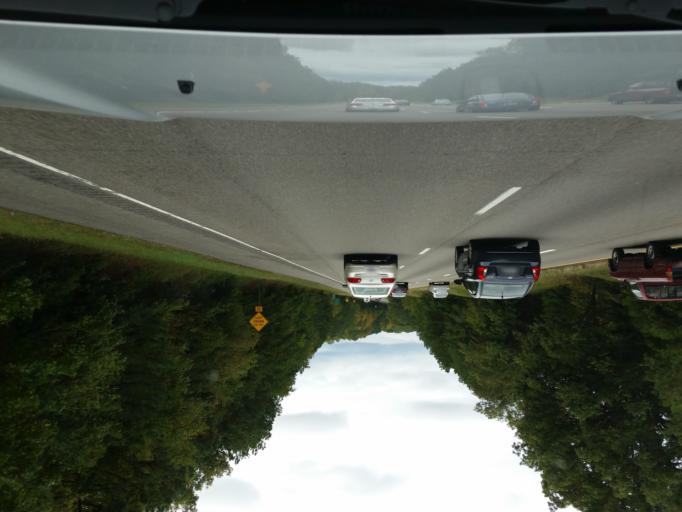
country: US
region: Virginia
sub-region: Henrico County
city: Sandston
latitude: 37.5158
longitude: -77.2521
